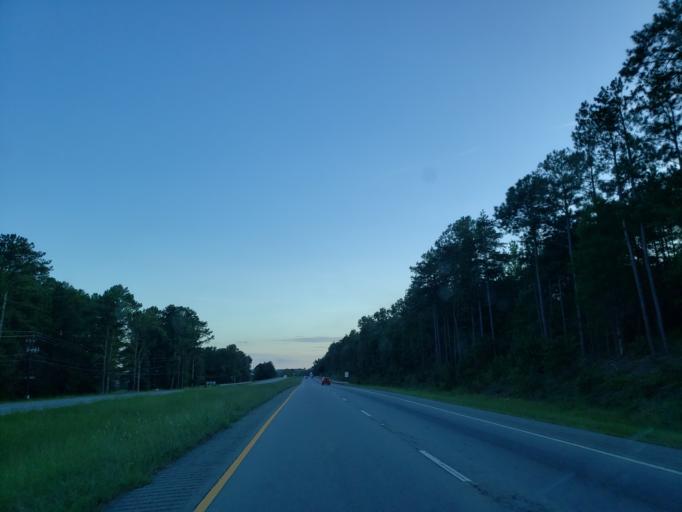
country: US
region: Georgia
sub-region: Floyd County
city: Lindale
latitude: 34.2087
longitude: -85.1911
